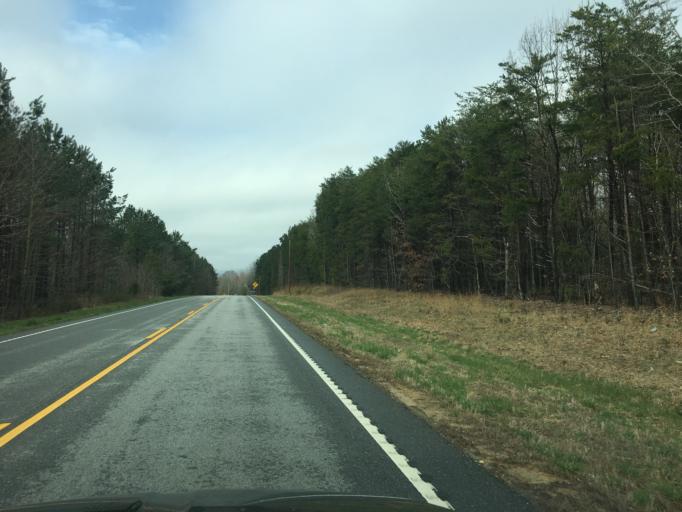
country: US
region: South Carolina
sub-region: Spartanburg County
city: Landrum
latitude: 35.1153
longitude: -82.2405
